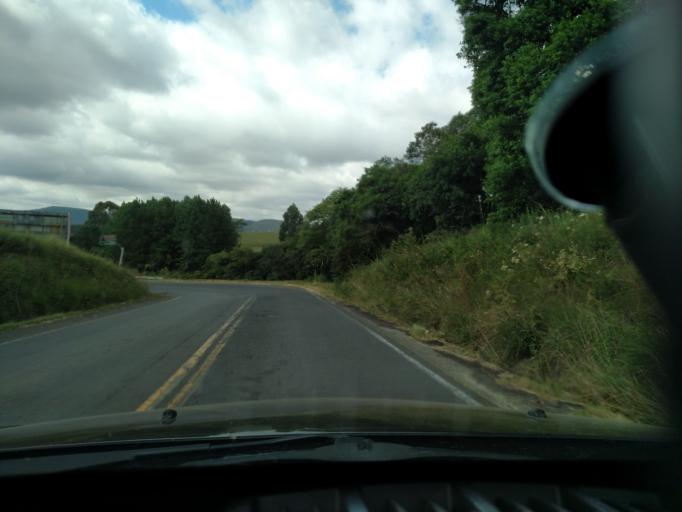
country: BR
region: Santa Catarina
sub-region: Lages
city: Lages
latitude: -27.8253
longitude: -50.2507
